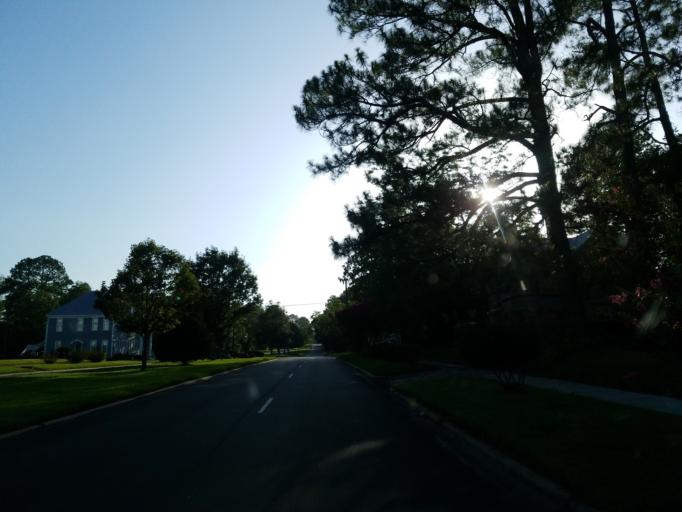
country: US
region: Georgia
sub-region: Ben Hill County
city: Fitzgerald
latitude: 31.7149
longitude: -83.2603
